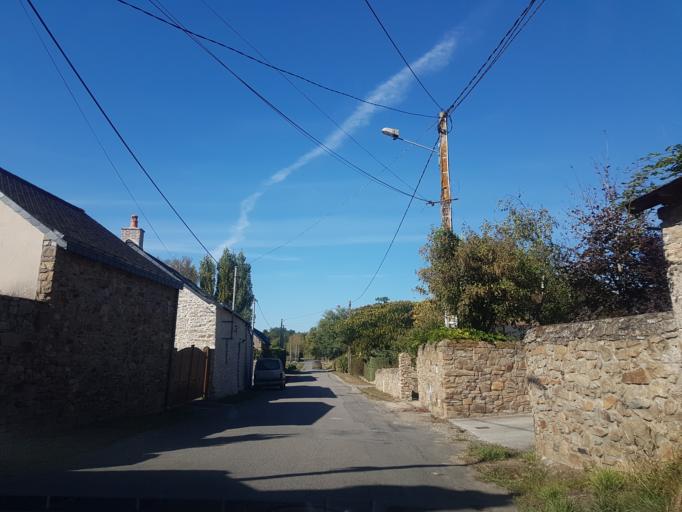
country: FR
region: Pays de la Loire
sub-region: Departement de la Loire-Atlantique
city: Petit-Mars
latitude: 47.3944
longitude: -1.4625
